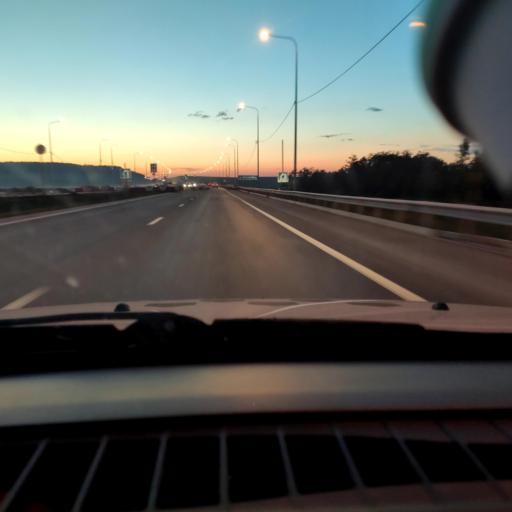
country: RU
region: Sverdlovsk
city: Aramil
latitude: 56.6505
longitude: 60.8042
